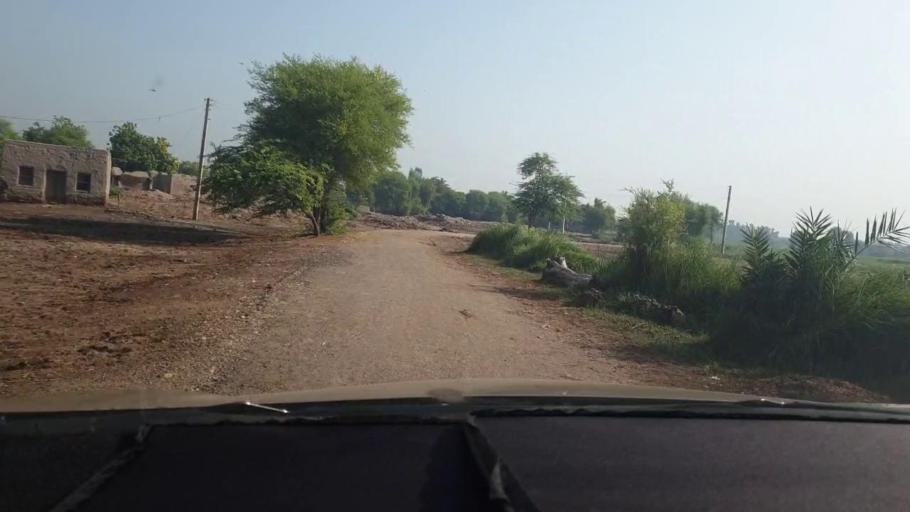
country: PK
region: Sindh
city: Kambar
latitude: 27.6015
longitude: 68.1119
